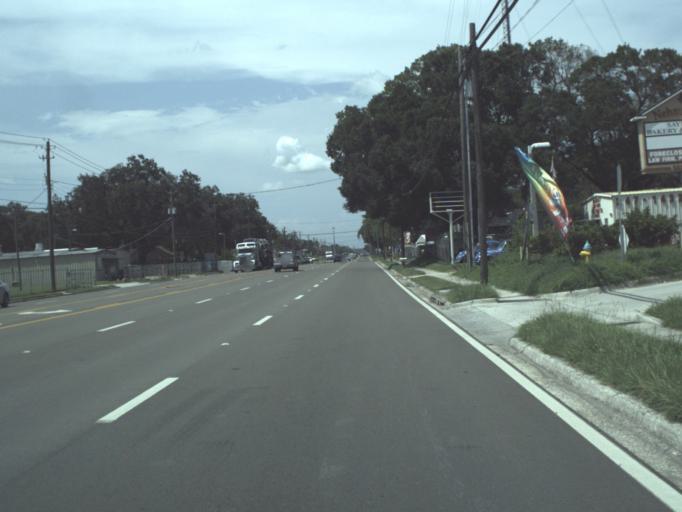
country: US
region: Florida
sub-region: Hillsborough County
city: Palm River-Clair Mel
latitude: 27.9290
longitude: -82.4018
